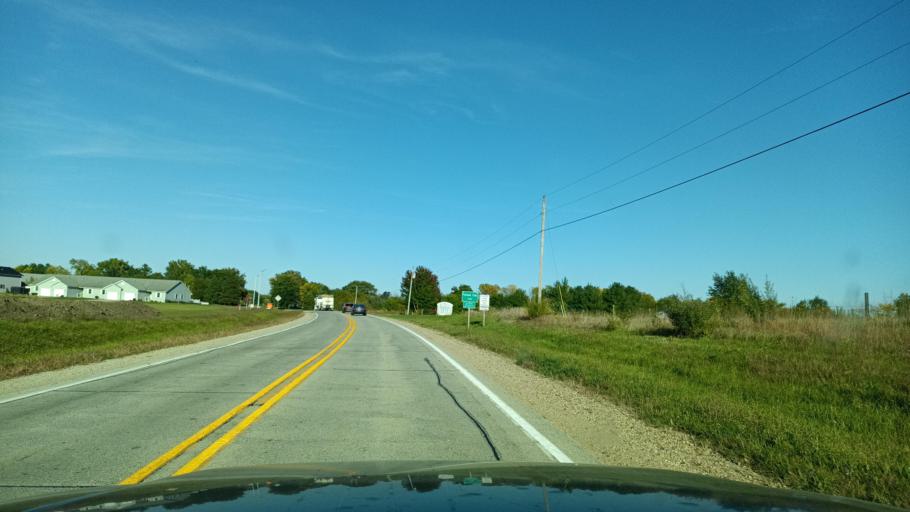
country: US
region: Illinois
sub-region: De Witt County
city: Farmer City
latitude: 40.2328
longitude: -88.6596
